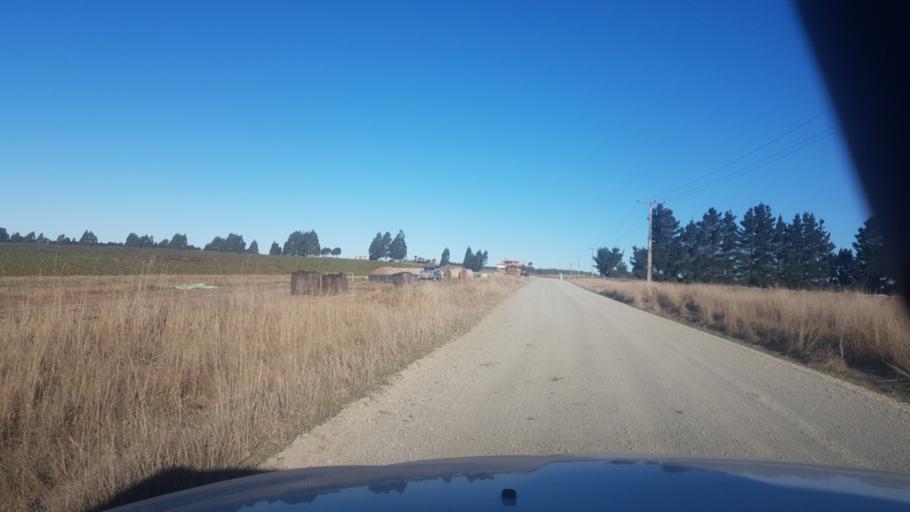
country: NZ
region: Canterbury
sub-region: Timaru District
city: Pleasant Point
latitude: -44.3566
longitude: 171.0691
